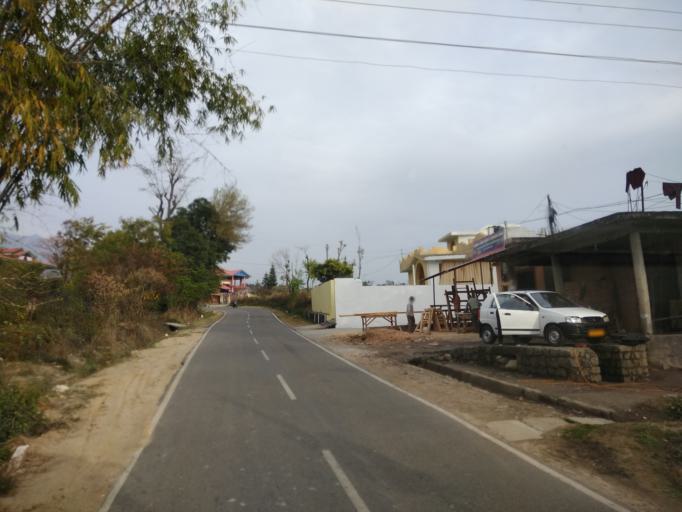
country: IN
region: Himachal Pradesh
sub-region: Kangra
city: Palampur
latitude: 32.1100
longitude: 76.4955
